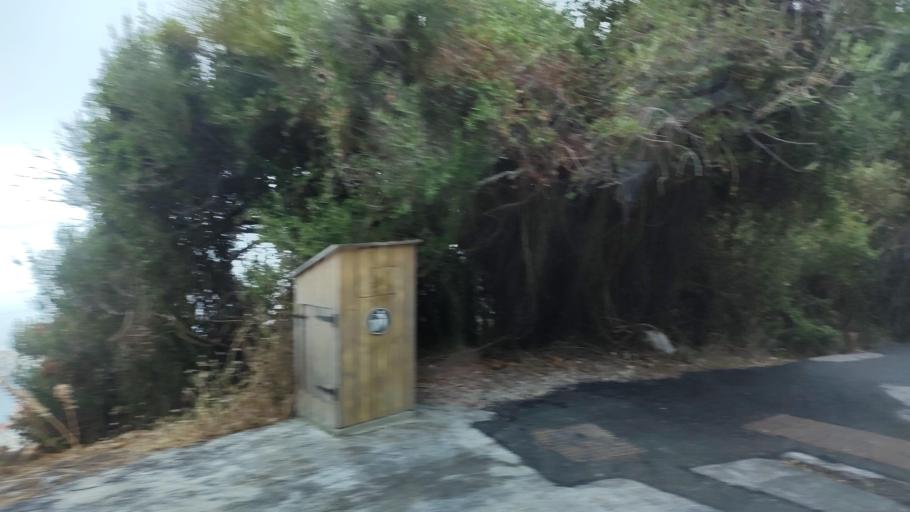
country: GI
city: Gibraltar
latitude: 36.1359
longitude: -5.3496
